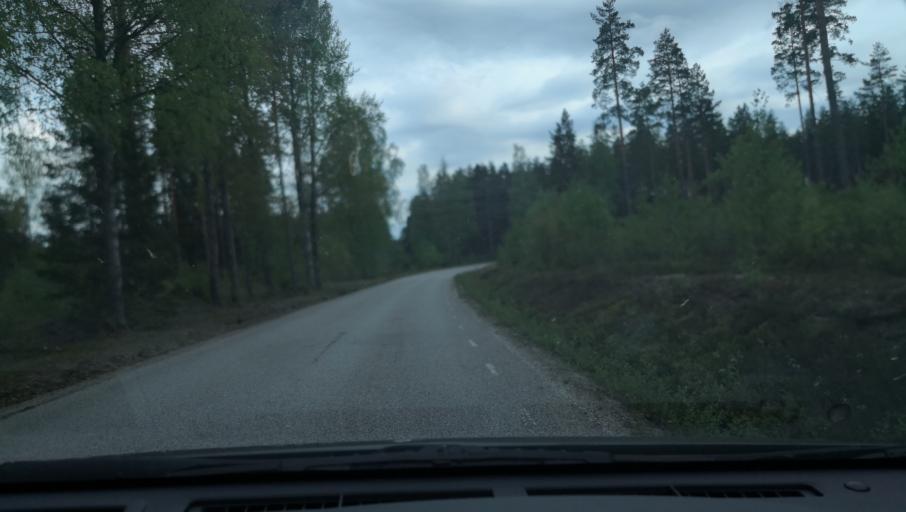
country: SE
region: Vaestmanland
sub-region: Skinnskattebergs Kommun
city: Skinnskatteberg
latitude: 59.8127
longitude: 15.5578
